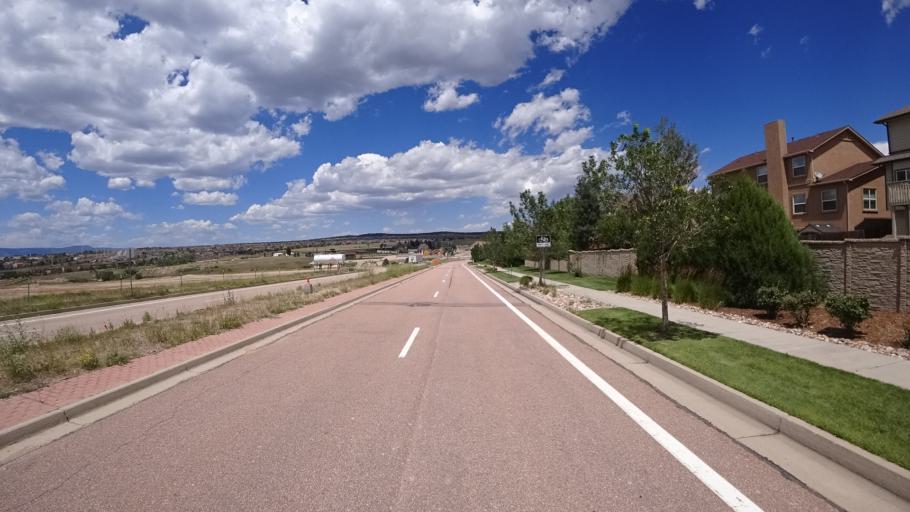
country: US
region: Colorado
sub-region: El Paso County
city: Black Forest
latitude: 38.9474
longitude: -104.7147
